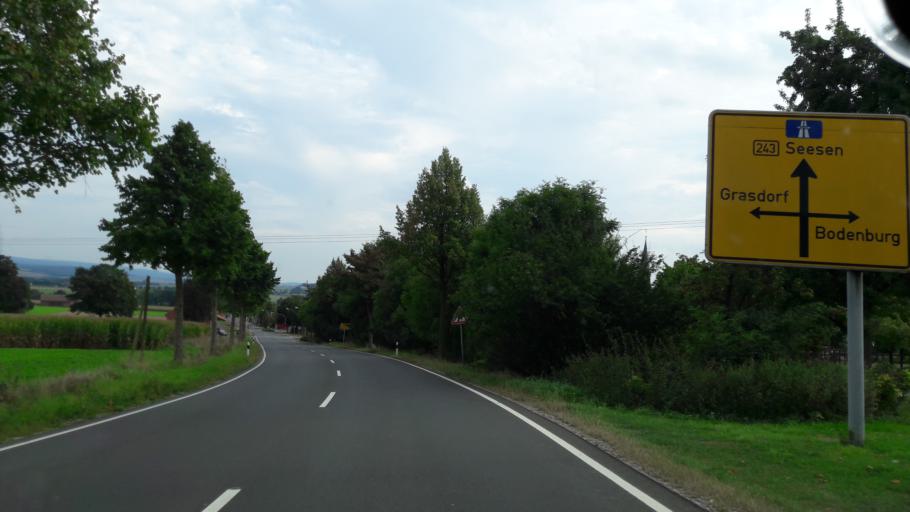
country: DE
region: Lower Saxony
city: Bockenem
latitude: 52.0401
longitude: 10.0842
